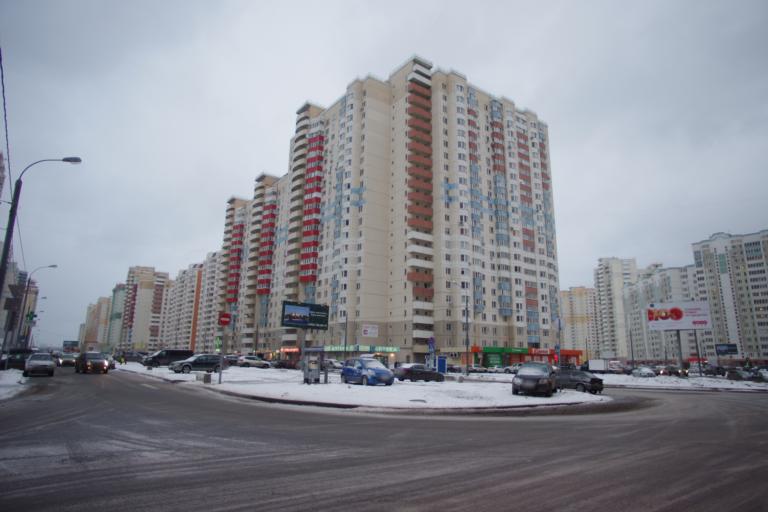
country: RU
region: Moskovskaya
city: Pavshino
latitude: 55.8190
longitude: 37.3632
